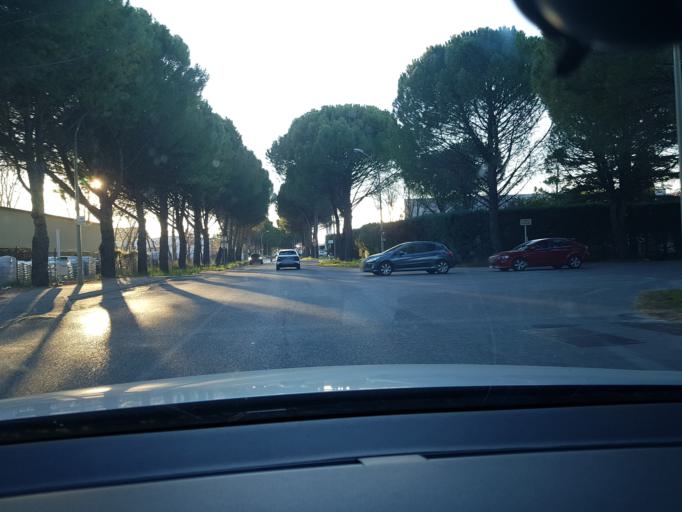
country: FR
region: Provence-Alpes-Cote d'Azur
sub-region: Departement des Bouches-du-Rhone
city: Rousset
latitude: 43.4691
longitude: 5.6083
